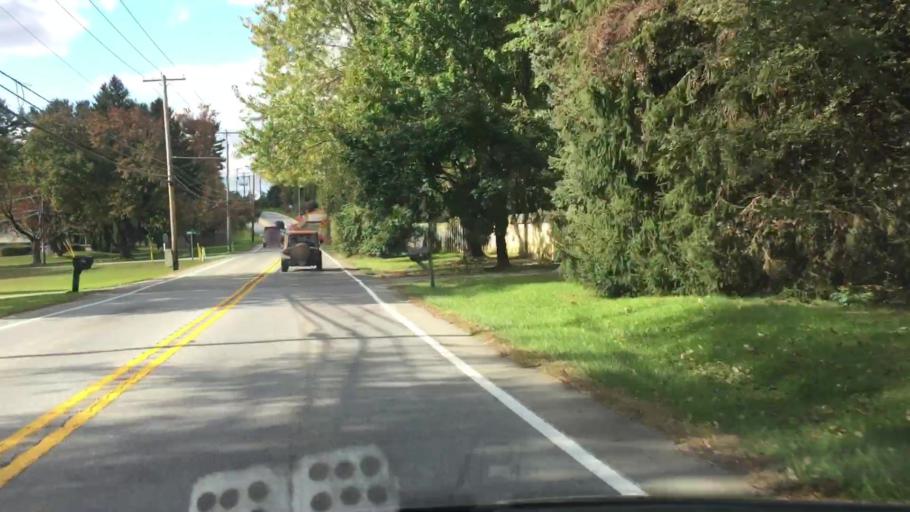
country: US
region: Pennsylvania
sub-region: Chester County
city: West Chester
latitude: 39.9964
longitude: -75.5632
